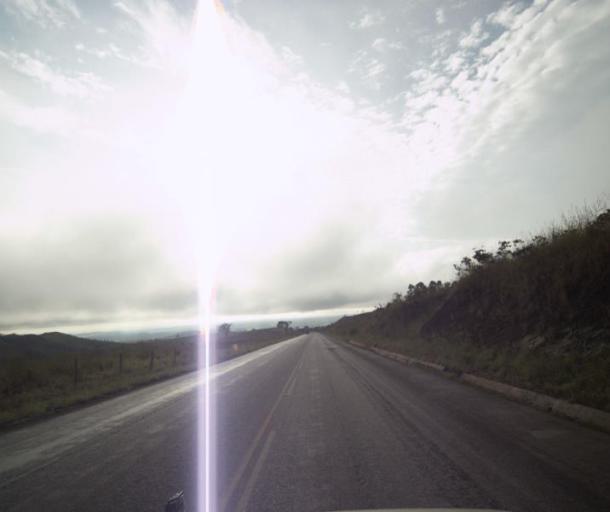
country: BR
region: Goias
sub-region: Pirenopolis
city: Pirenopolis
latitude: -15.7527
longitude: -48.7471
